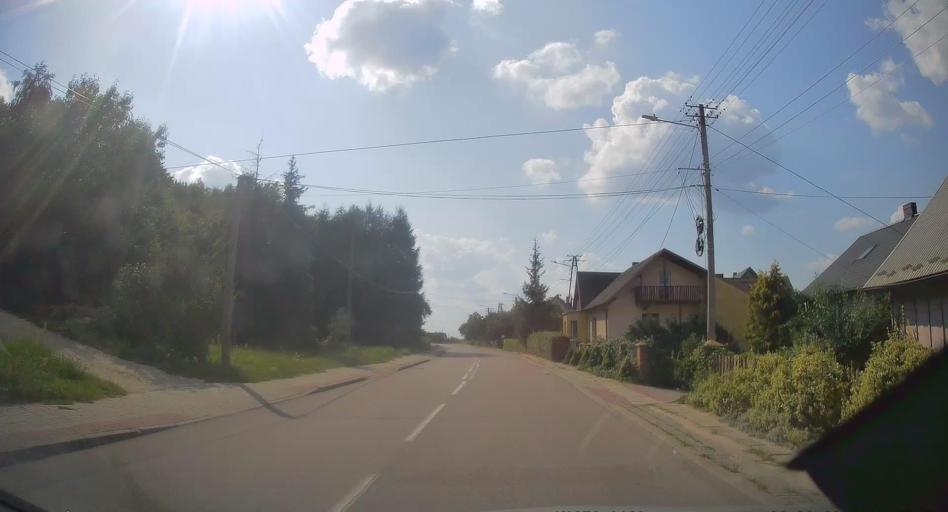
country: PL
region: Swietokrzyskie
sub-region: Powiat jedrzejowski
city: Malogoszcz
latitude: 50.8683
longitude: 20.2815
